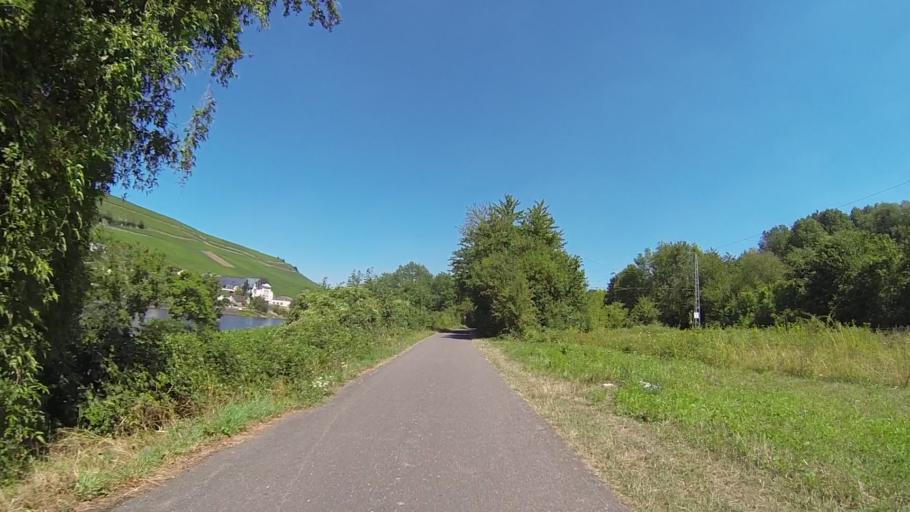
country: LU
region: Grevenmacher
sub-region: Canton de Grevenmacher
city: Wormeldange
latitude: 49.6112
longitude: 6.4096
